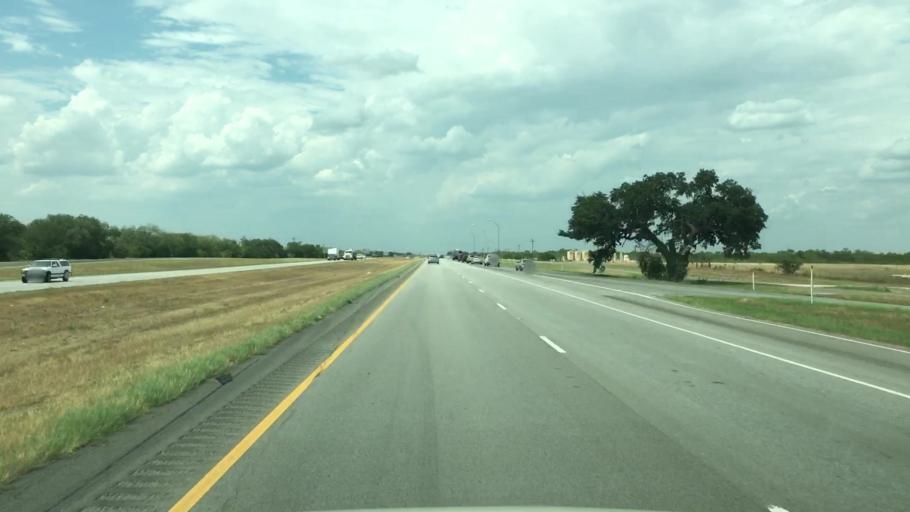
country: US
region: Texas
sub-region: Live Oak County
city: Three Rivers
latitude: 28.5330
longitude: -98.1883
